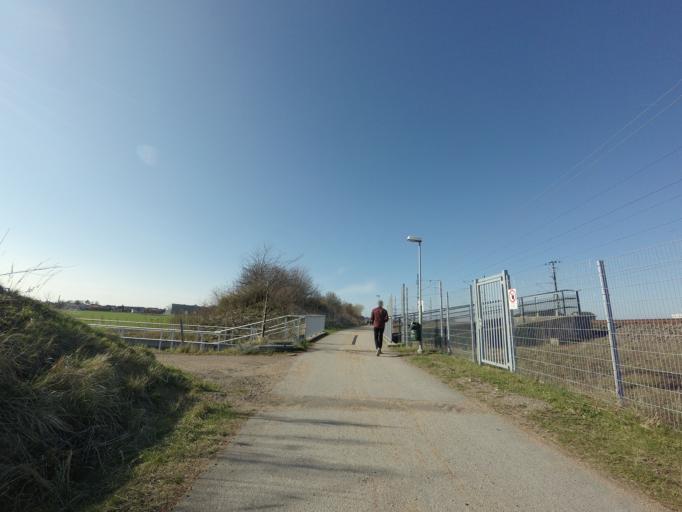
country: SE
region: Skane
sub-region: Landskrona
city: Landskrona
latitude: 55.8759
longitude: 12.8595
